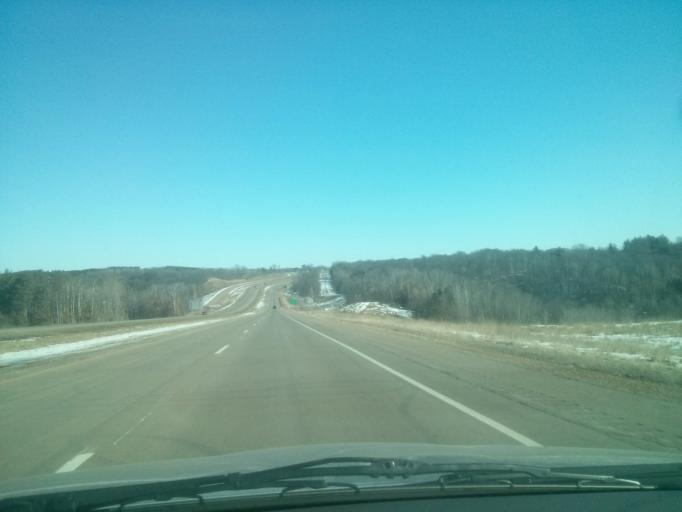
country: US
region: Wisconsin
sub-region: Saint Croix County
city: Somerset
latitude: 45.0966
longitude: -92.7349
